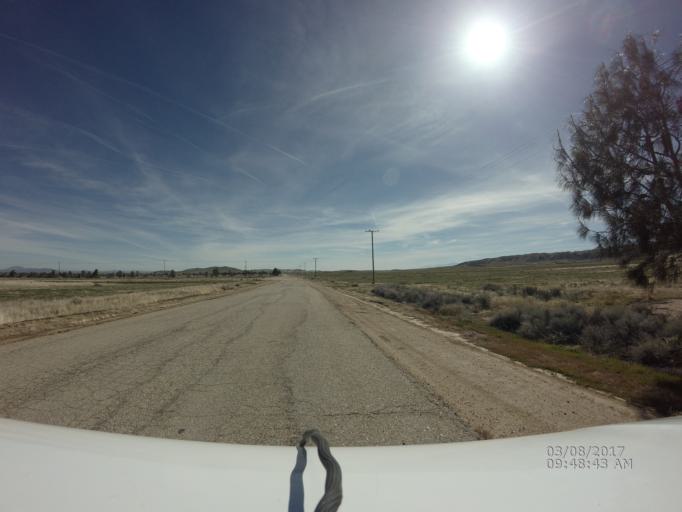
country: US
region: California
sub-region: Los Angeles County
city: Green Valley
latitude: 34.7388
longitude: -118.4679
